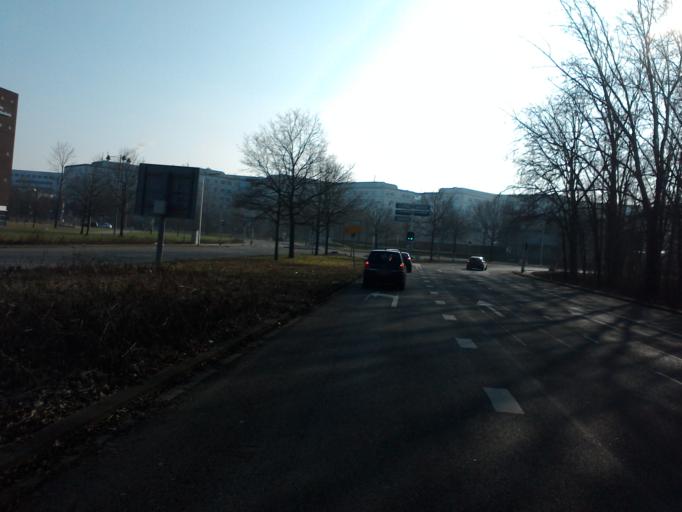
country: NL
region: Utrecht
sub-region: Gemeente De Bilt
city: De Bilt
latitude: 52.0899
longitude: 5.1794
